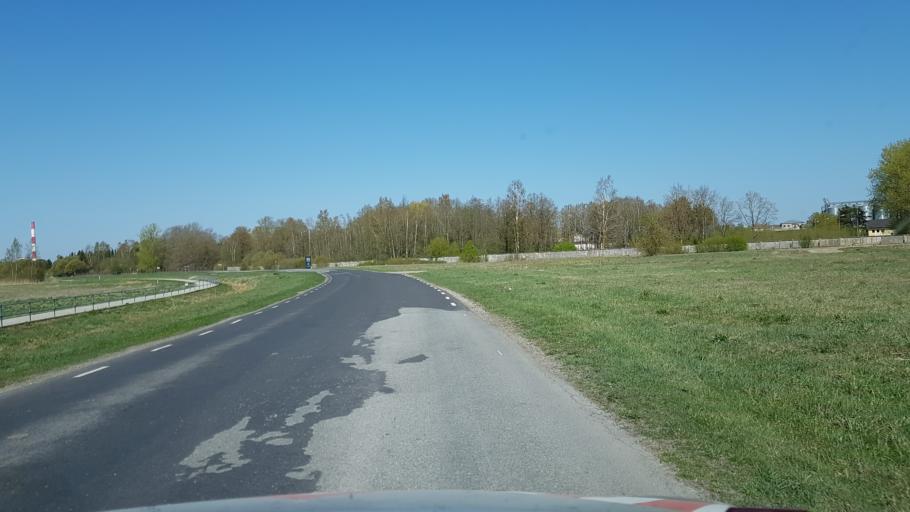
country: EE
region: Harju
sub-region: Joelaehtme vald
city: Loo
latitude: 59.4257
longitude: 24.9447
